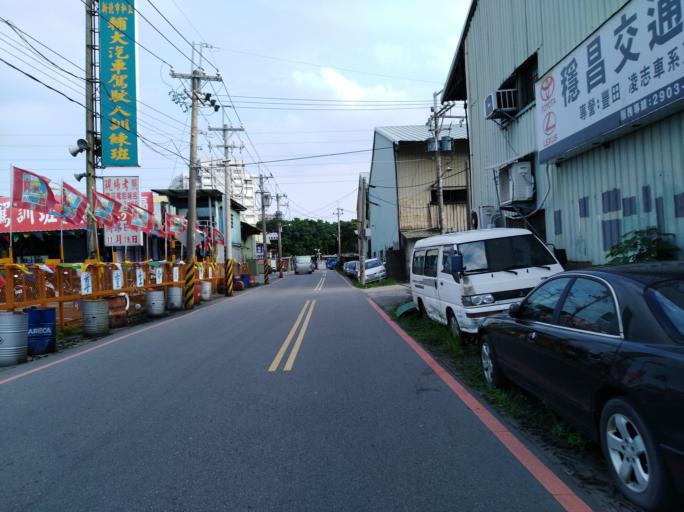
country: TW
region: Taipei
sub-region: Taipei
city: Banqiao
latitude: 25.0365
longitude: 121.4278
